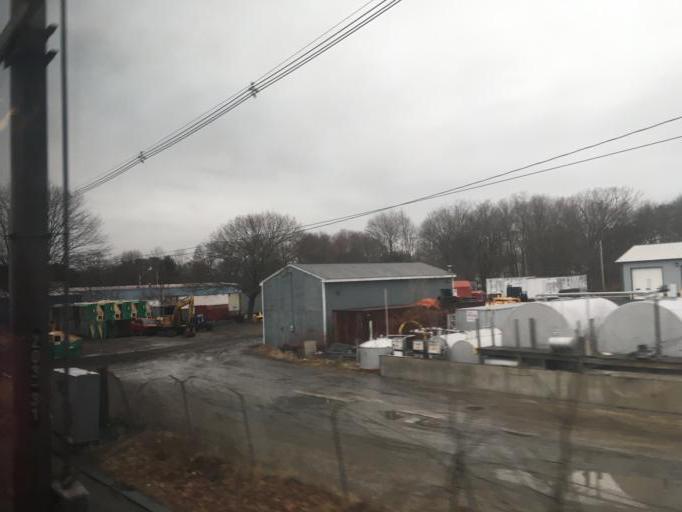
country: US
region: Massachusetts
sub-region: Bristol County
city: Mansfield
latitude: 42.0288
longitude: -71.2228
